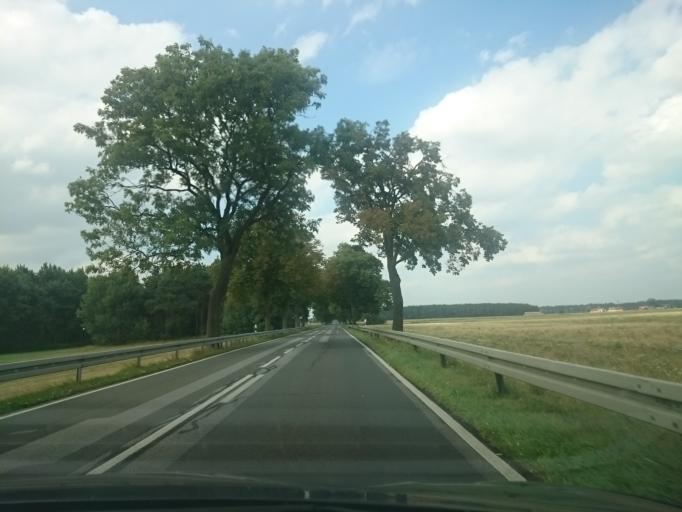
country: DE
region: Mecklenburg-Vorpommern
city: Ferdinandshof
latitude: 53.6862
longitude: 13.8815
